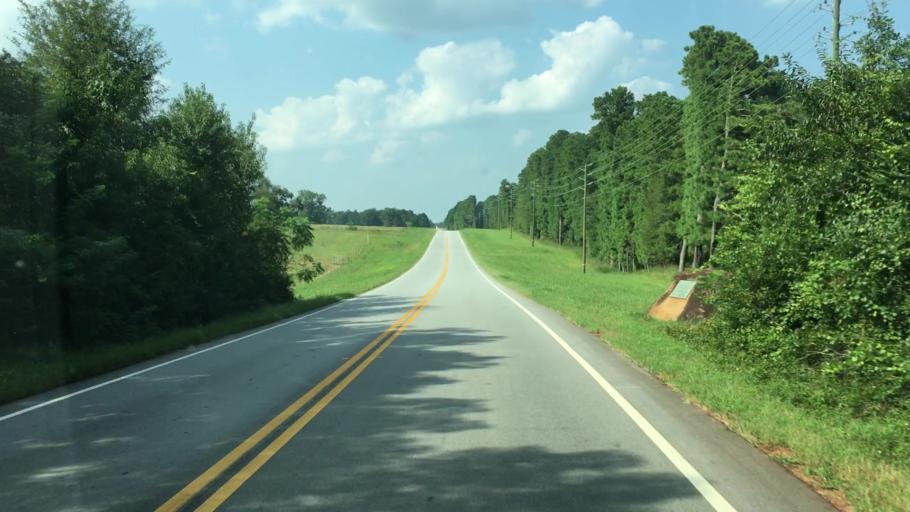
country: US
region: Georgia
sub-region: Jasper County
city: Monticello
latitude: 33.4555
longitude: -83.7532
